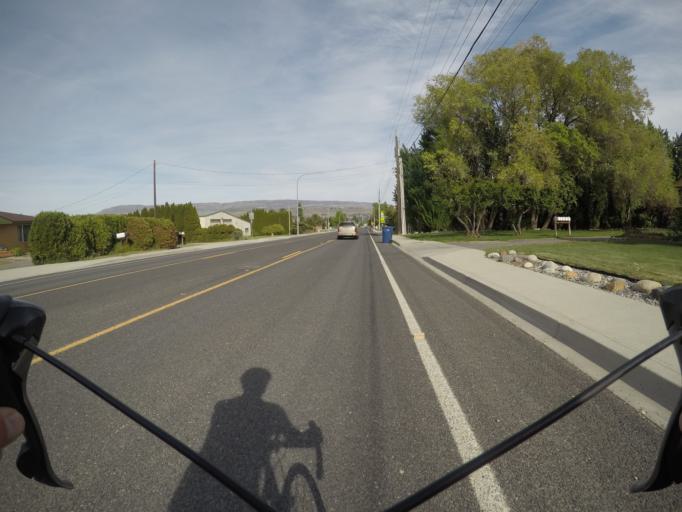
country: US
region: Washington
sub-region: Chelan County
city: West Wenatchee
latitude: 47.4424
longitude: -120.3386
